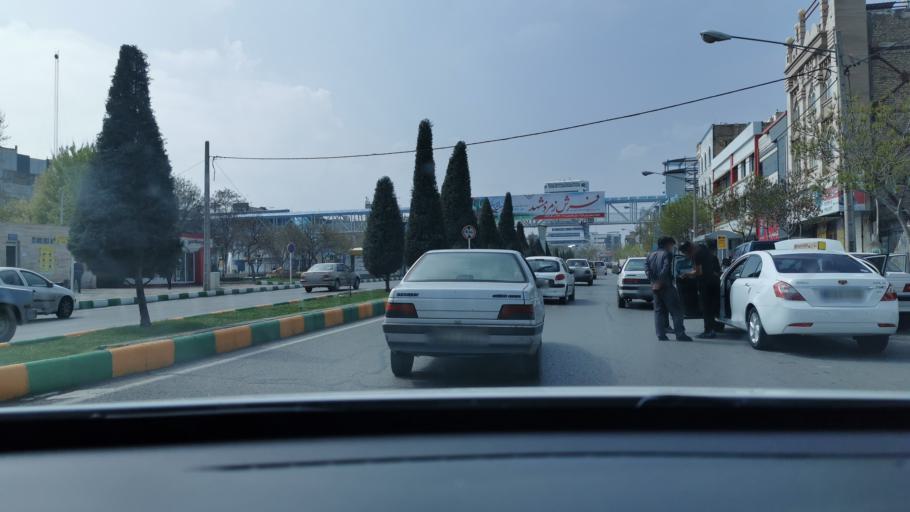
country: IR
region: Razavi Khorasan
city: Mashhad
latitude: 36.3290
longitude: 59.5282
